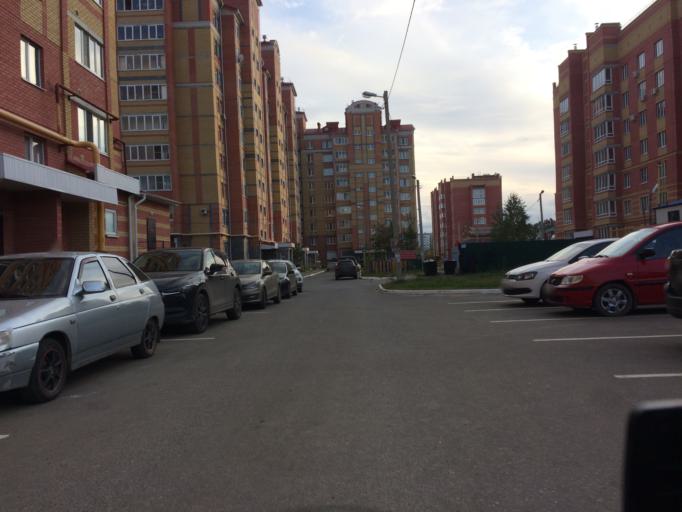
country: RU
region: Mariy-El
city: Yoshkar-Ola
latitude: 56.6354
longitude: 47.9141
